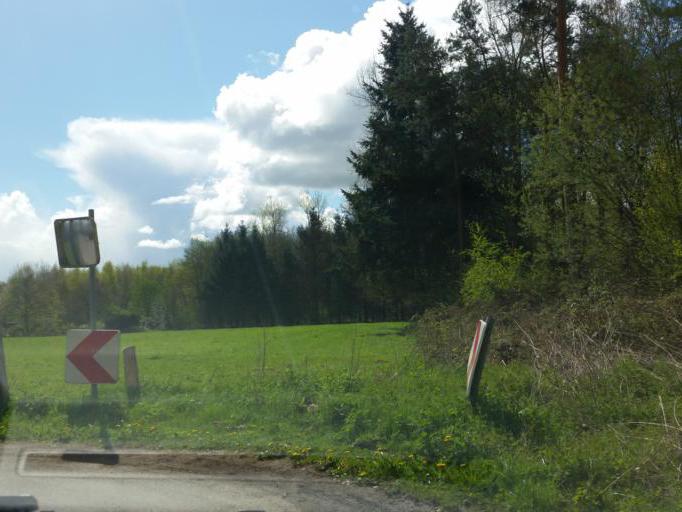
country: BE
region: Flanders
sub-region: Provincie Vlaams-Brabant
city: Kampenhout
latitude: 50.9749
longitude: 4.5298
